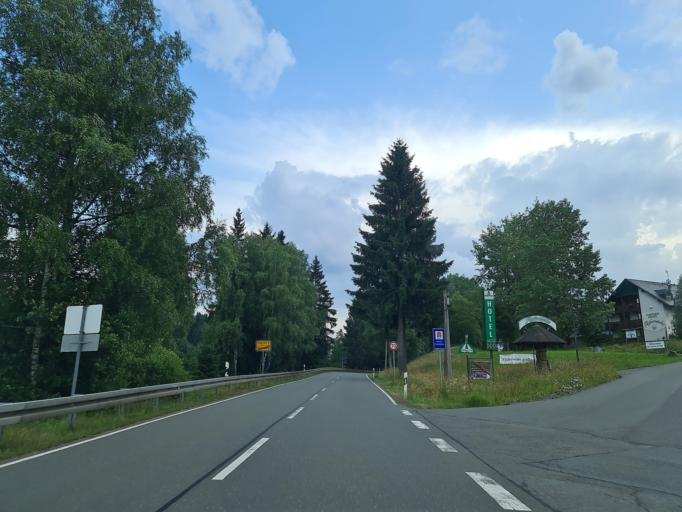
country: DE
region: Saxony
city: Hammerbrucke
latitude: 50.4162
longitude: 12.4016
